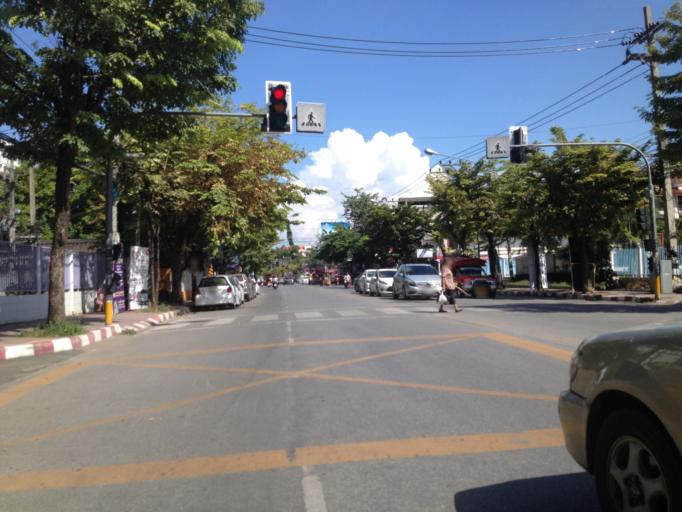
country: TH
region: Chiang Mai
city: Chiang Mai
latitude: 18.7894
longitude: 98.9685
